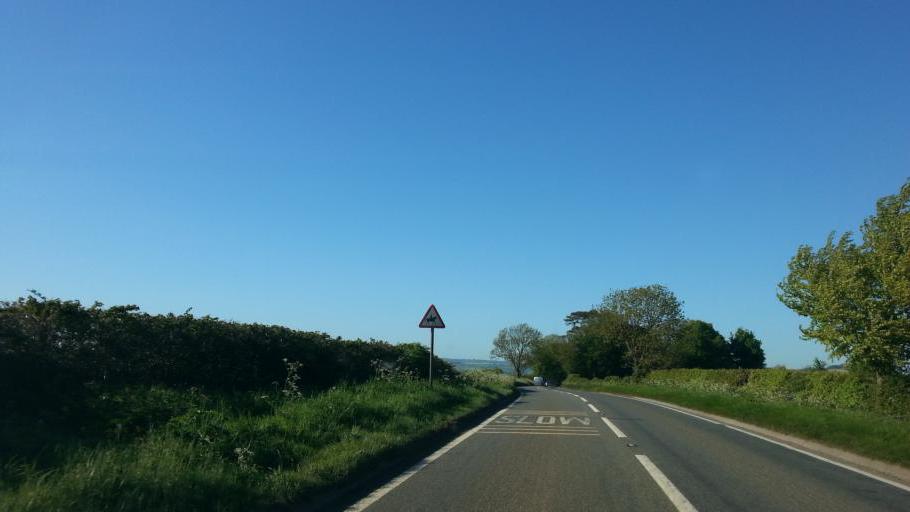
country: GB
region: England
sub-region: Somerset
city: Castle Cary
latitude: 51.0847
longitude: -2.5057
